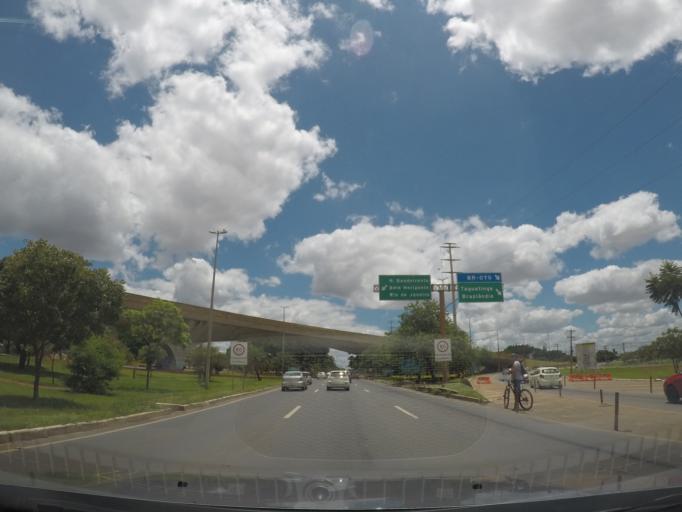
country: BR
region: Federal District
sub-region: Brasilia
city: Brasilia
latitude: -15.7845
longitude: -47.9412
